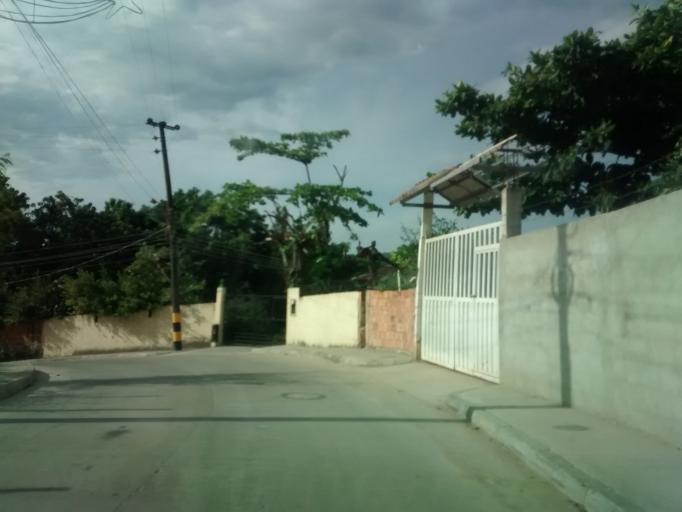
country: CO
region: Tolima
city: Melgar
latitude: 4.2094
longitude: -74.6296
